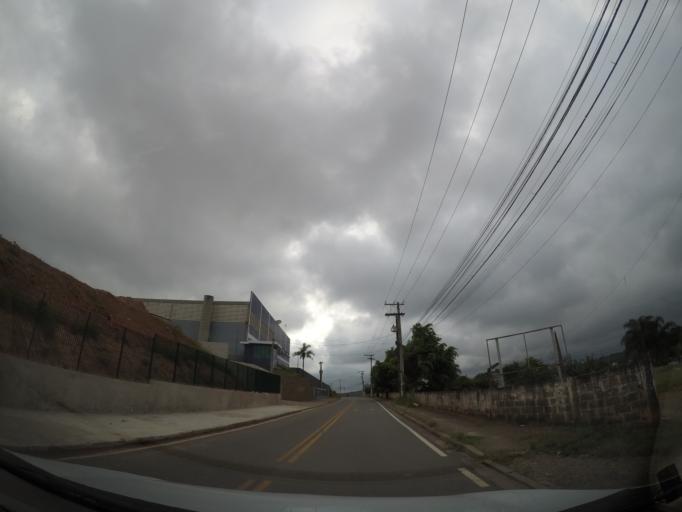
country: BR
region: Sao Paulo
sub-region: Aruja
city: Aruja
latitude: -23.4041
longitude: -46.3566
